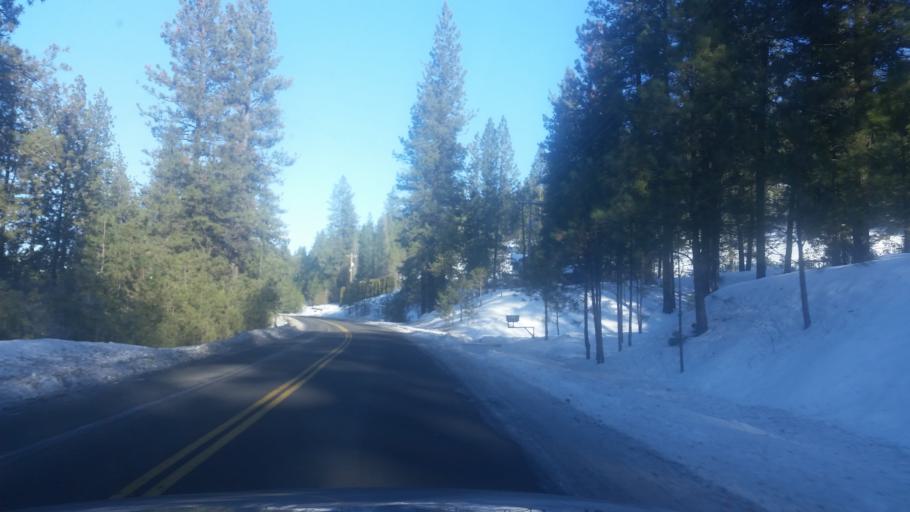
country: US
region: Washington
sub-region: Spokane County
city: Spokane
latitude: 47.6038
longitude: -117.4352
